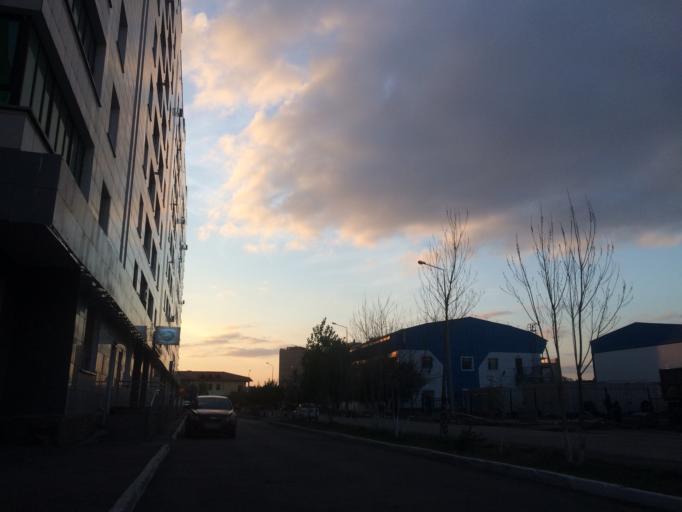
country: KZ
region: Astana Qalasy
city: Astana
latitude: 51.1428
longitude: 71.4135
